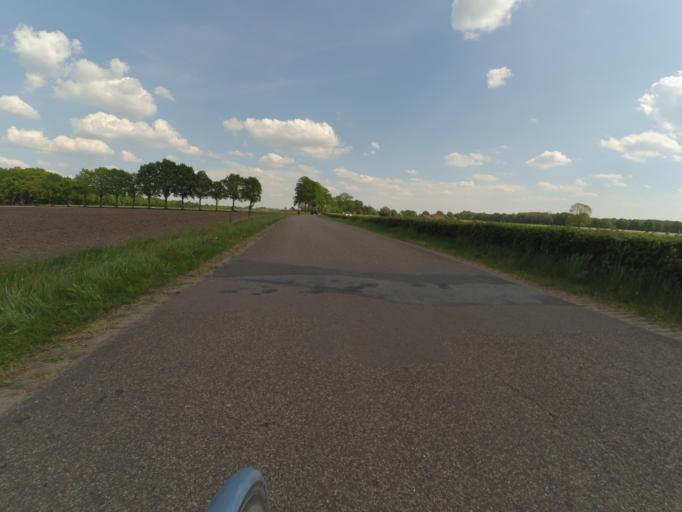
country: NL
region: Overijssel
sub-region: Gemeente Oldenzaal
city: Oldenzaal
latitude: 52.3412
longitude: 6.8663
